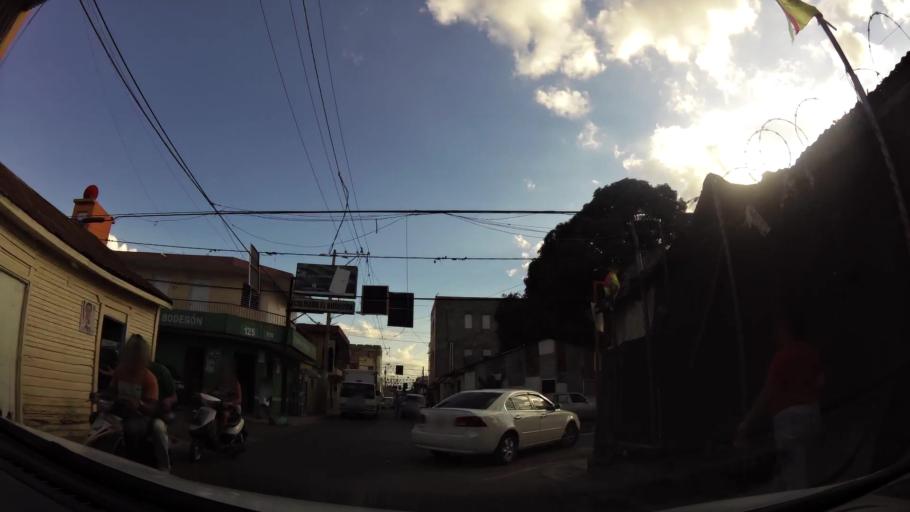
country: DO
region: Santiago
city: Santiago de los Caballeros
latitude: 19.4616
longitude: -70.7057
